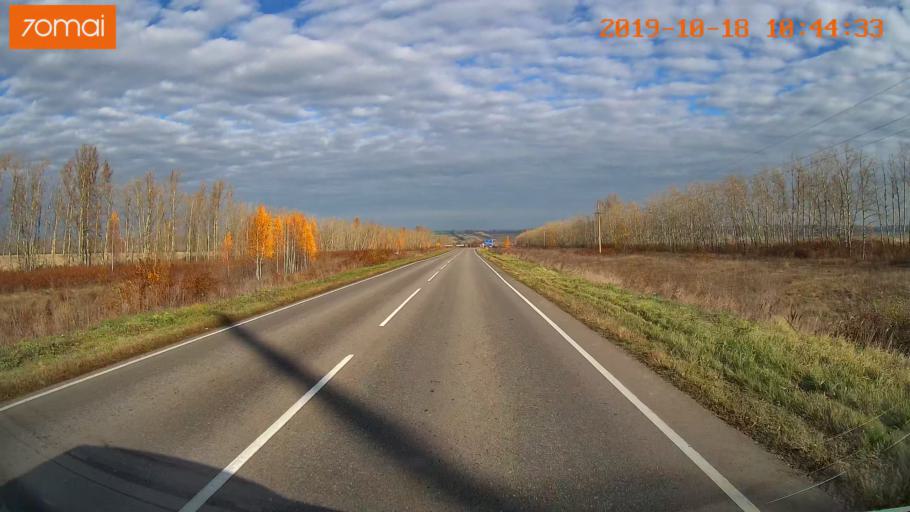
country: RU
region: Tula
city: Yepifan'
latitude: 53.6572
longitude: 38.6829
